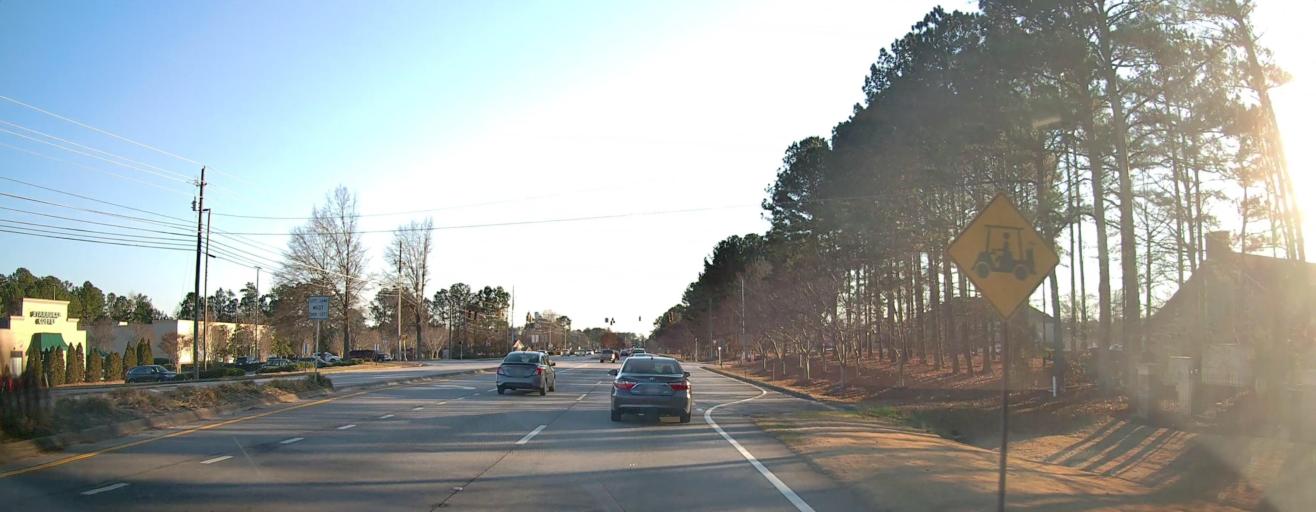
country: US
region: Georgia
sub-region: Fayette County
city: Peachtree City
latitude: 33.4233
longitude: -84.5586
